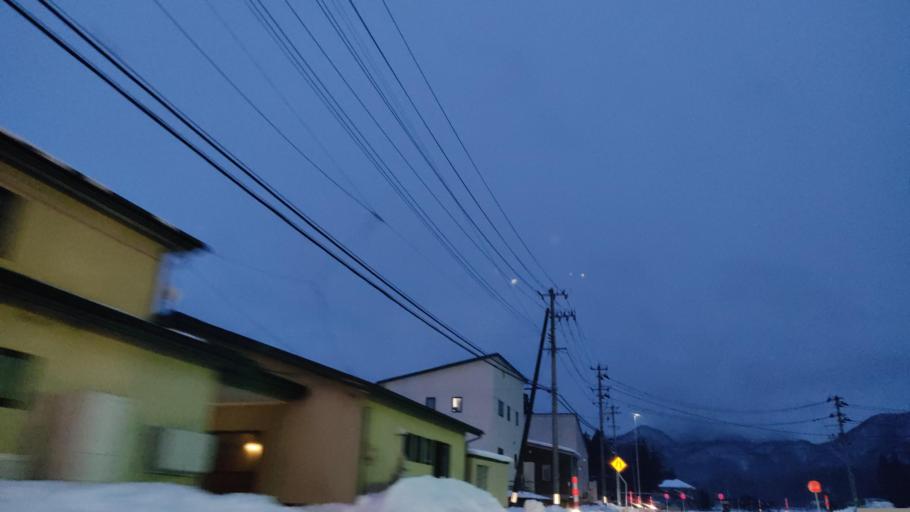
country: JP
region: Iwate
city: Morioka-shi
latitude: 39.6290
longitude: 141.1115
